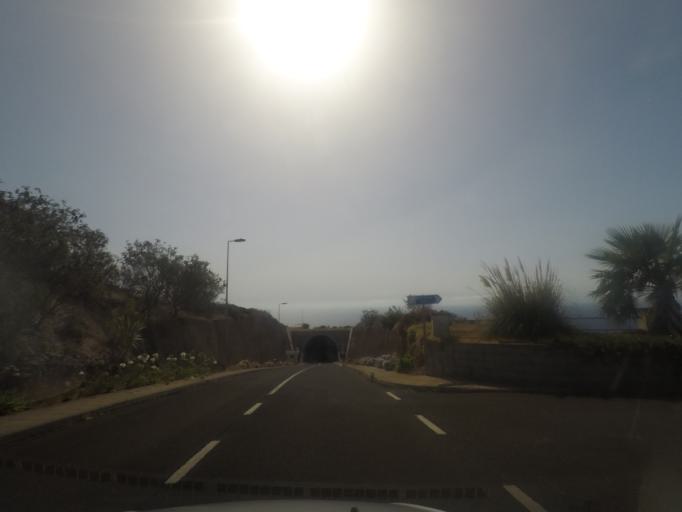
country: PT
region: Madeira
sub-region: Calheta
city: Faja da Ovelha
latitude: 32.8141
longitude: -17.2579
